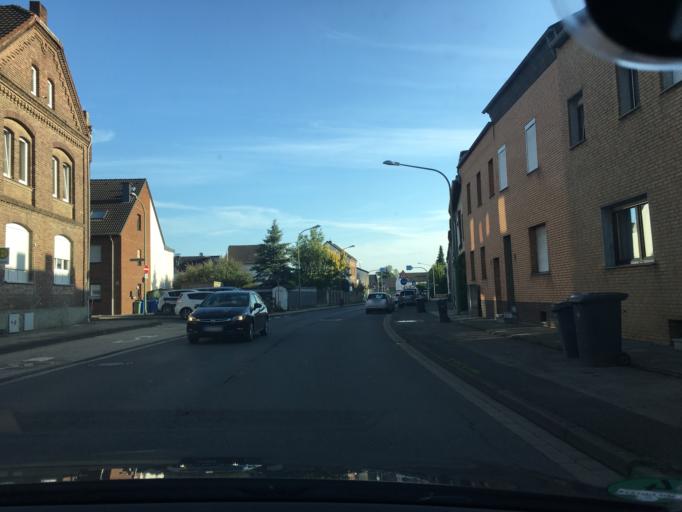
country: DE
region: North Rhine-Westphalia
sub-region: Regierungsbezirk Koln
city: Dueren
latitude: 50.8360
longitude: 6.4903
